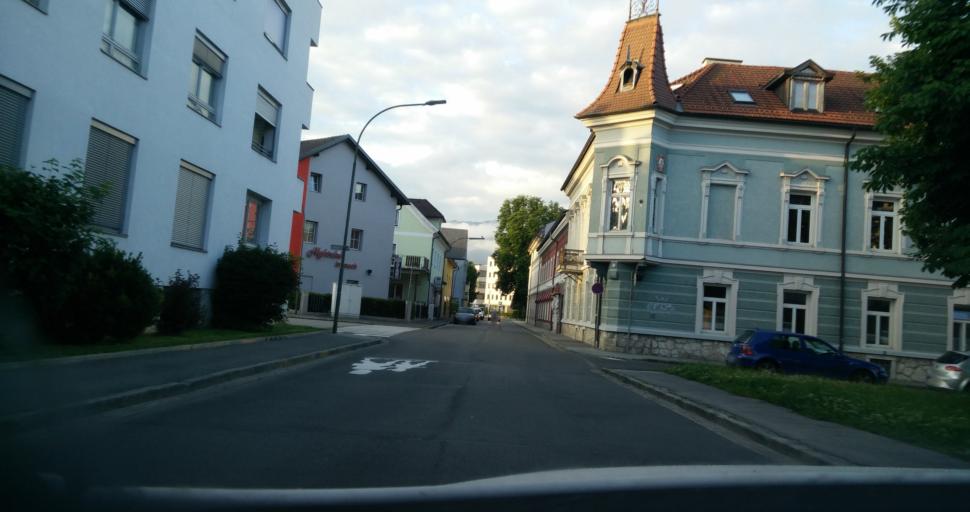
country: AT
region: Carinthia
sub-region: Villach Stadt
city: Villach
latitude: 46.6132
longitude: 13.8530
